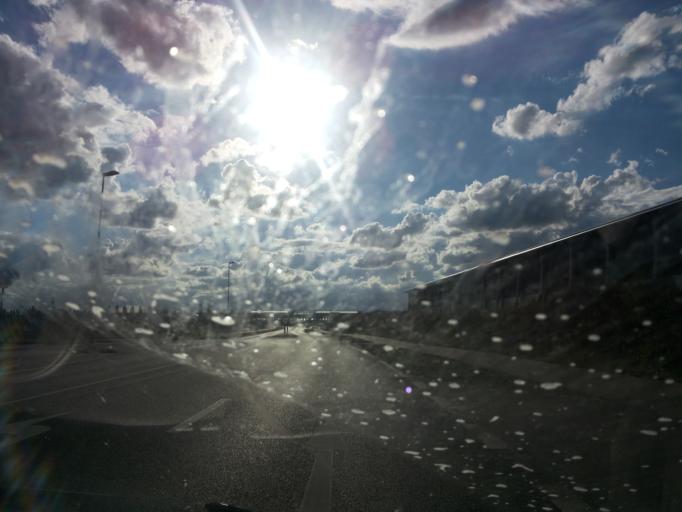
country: DE
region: Bavaria
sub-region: Upper Bavaria
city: Ingolstadt
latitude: 48.7786
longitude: 11.3985
